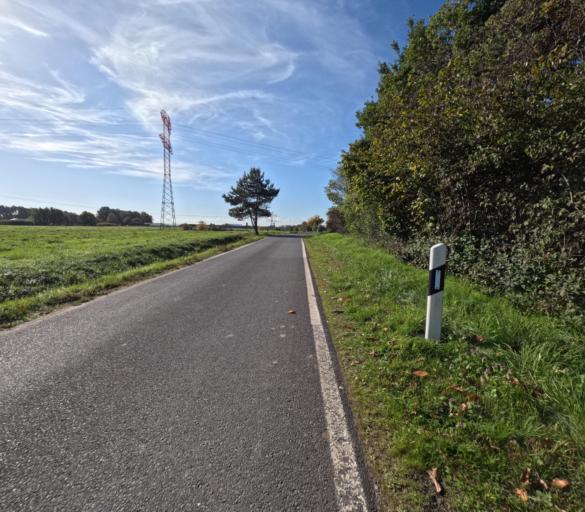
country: DE
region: Saxony
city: Ottendorf-Okrilla
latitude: 51.1568
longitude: 13.7813
